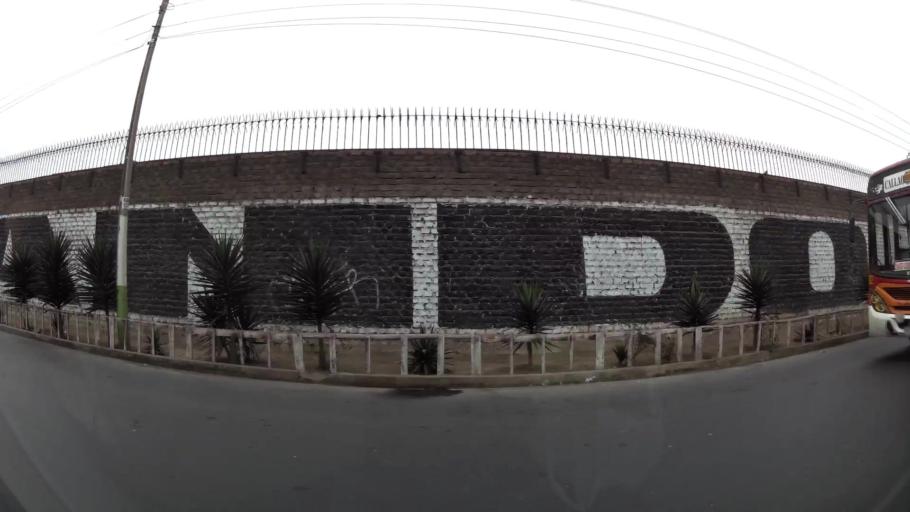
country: PE
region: Callao
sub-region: Callao
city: Callao
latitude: -12.0535
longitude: -77.1059
